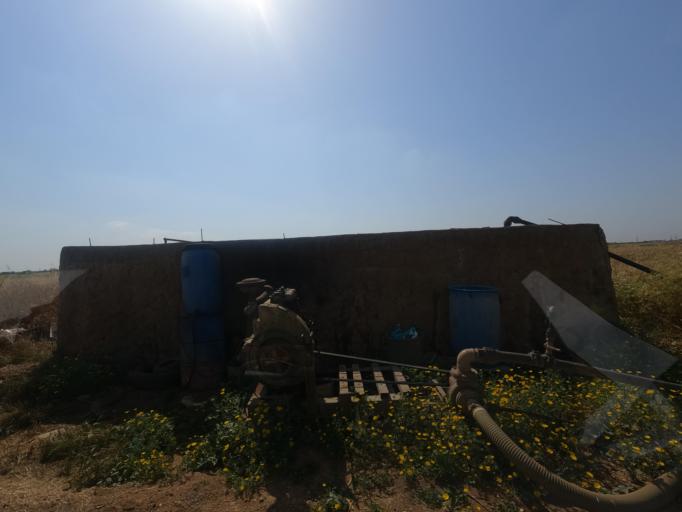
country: CY
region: Ammochostos
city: Avgorou
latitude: 35.0588
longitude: 33.8582
